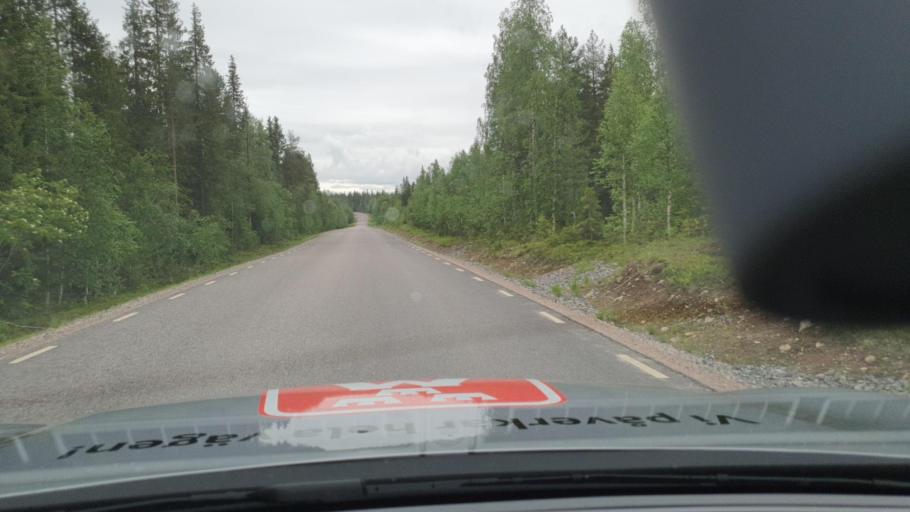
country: SE
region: Norrbotten
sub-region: Overtornea Kommun
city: OEvertornea
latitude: 66.5016
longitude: 23.4219
